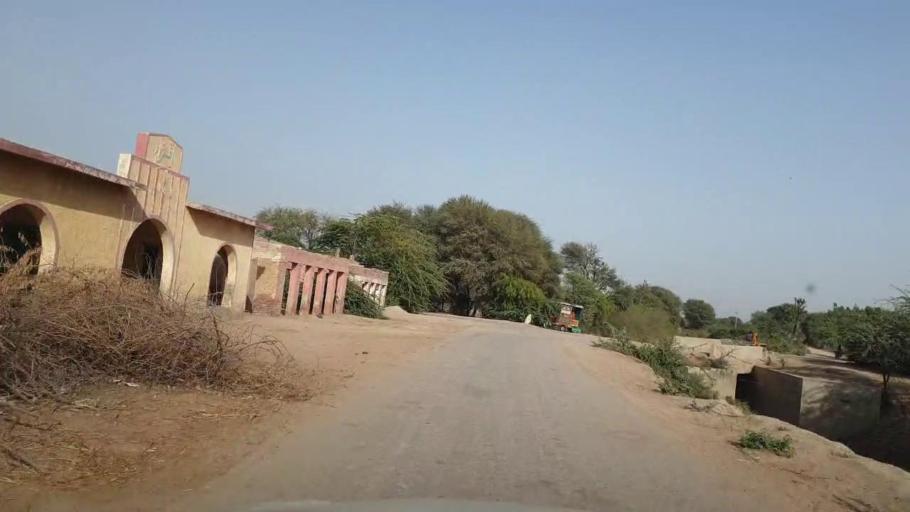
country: PK
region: Sindh
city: Tando Ghulam Ali
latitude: 25.0851
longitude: 68.8718
